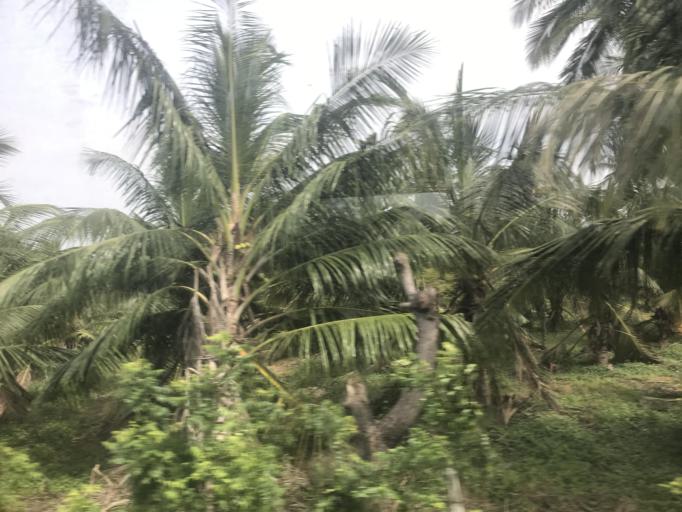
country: LK
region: Northern Province
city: Kilinochchi
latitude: 9.5901
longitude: 80.3468
